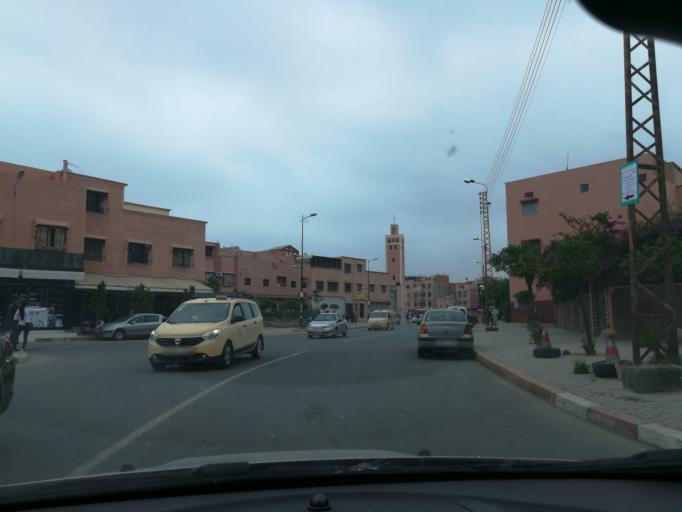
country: MA
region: Marrakech-Tensift-Al Haouz
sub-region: Marrakech
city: Marrakesh
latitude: 31.6600
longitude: -7.9976
